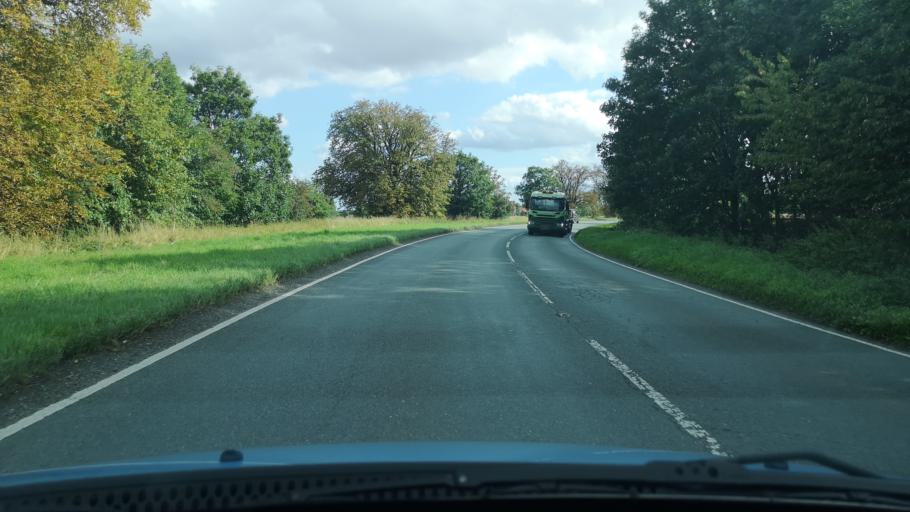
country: GB
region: England
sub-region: North Lincolnshire
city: Belton
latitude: 53.5769
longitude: -0.8184
